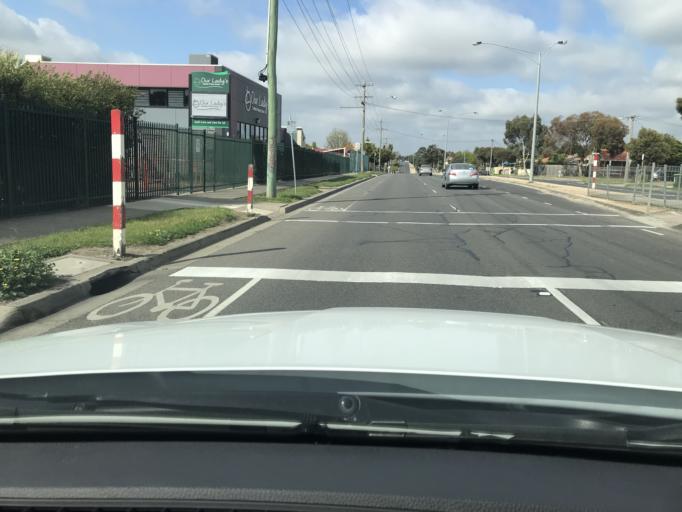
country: AU
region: Victoria
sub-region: Hume
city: Craigieburn
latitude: -37.5985
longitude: 144.9302
